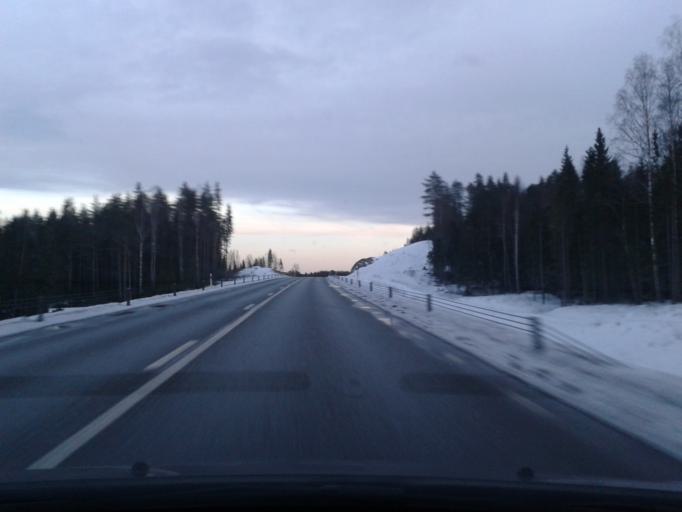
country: SE
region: Vaesternorrland
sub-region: Kramfors Kommun
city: Bollstabruk
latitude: 63.0657
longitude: 17.5864
